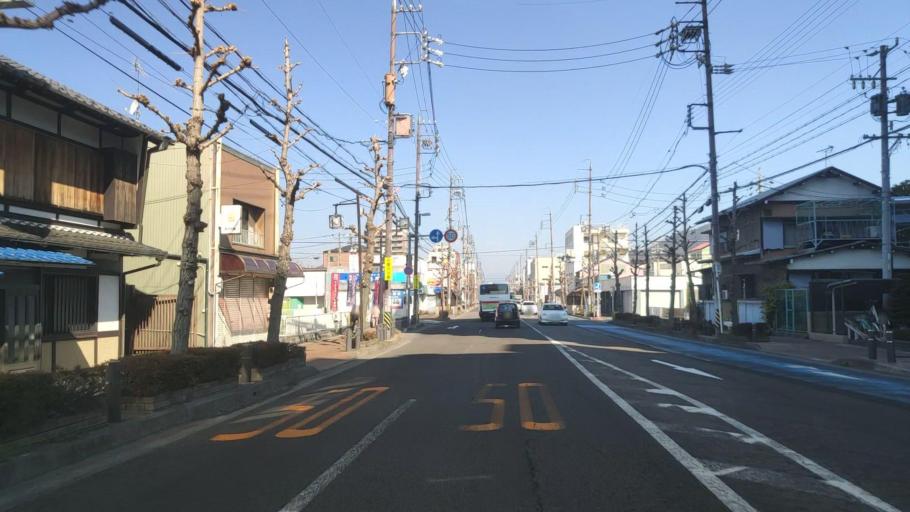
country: JP
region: Gifu
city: Gifu-shi
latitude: 35.4430
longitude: 136.7736
